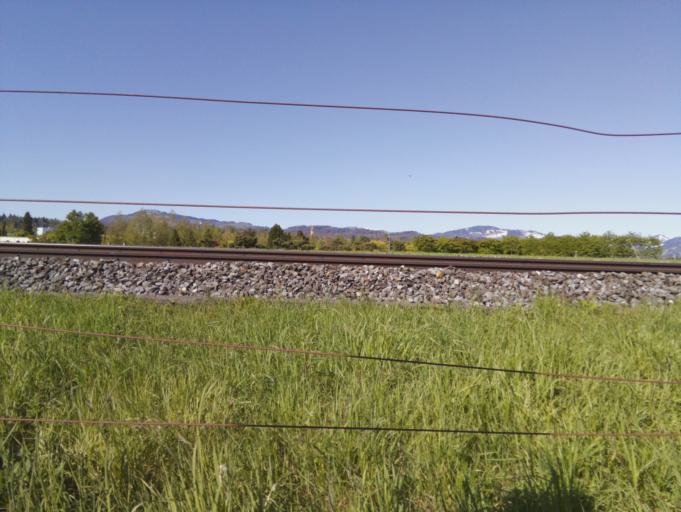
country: CH
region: Saint Gallen
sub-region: Wahlkreis See-Gaster
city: Jona
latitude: 47.2211
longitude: 8.8650
